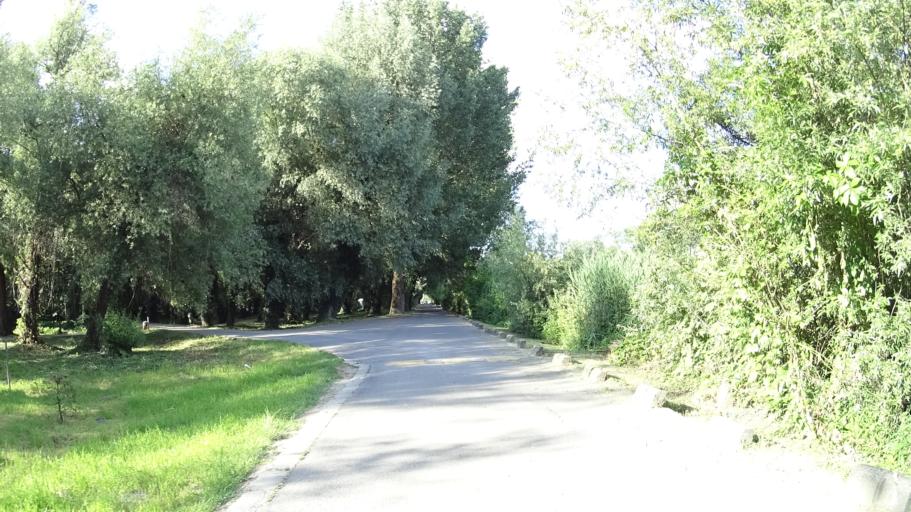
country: HU
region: Pest
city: Dunaharaszti
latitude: 47.3597
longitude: 19.0850
